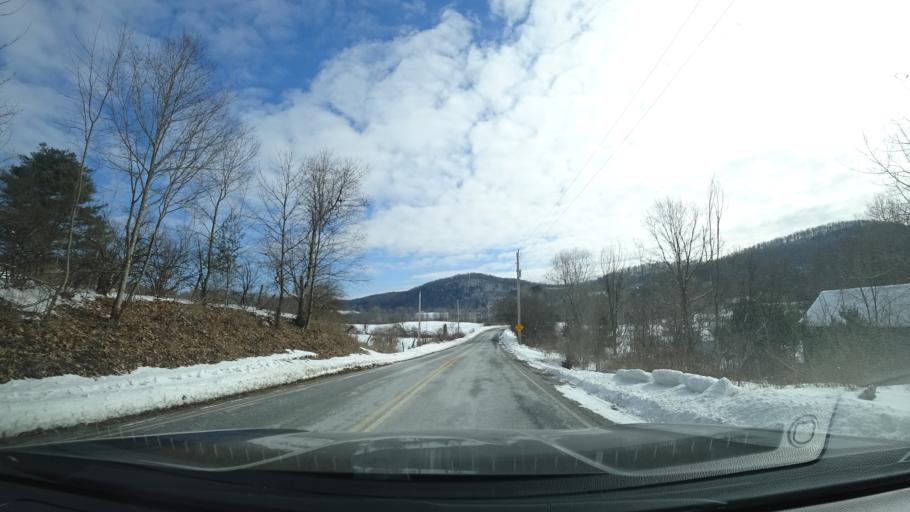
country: US
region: New York
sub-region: Washington County
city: Greenwich
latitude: 43.2430
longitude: -73.3845
